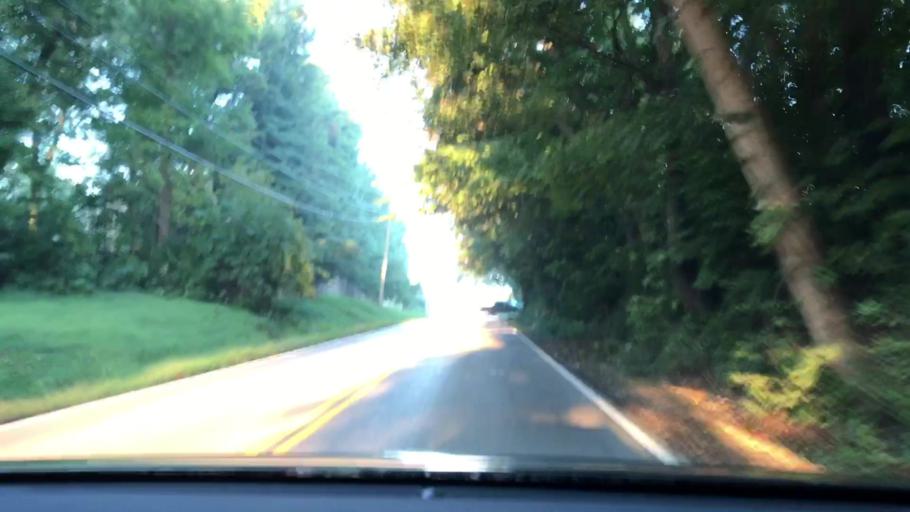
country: US
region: Tennessee
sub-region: Williamson County
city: Brentwood Estates
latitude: 36.0310
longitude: -86.7504
